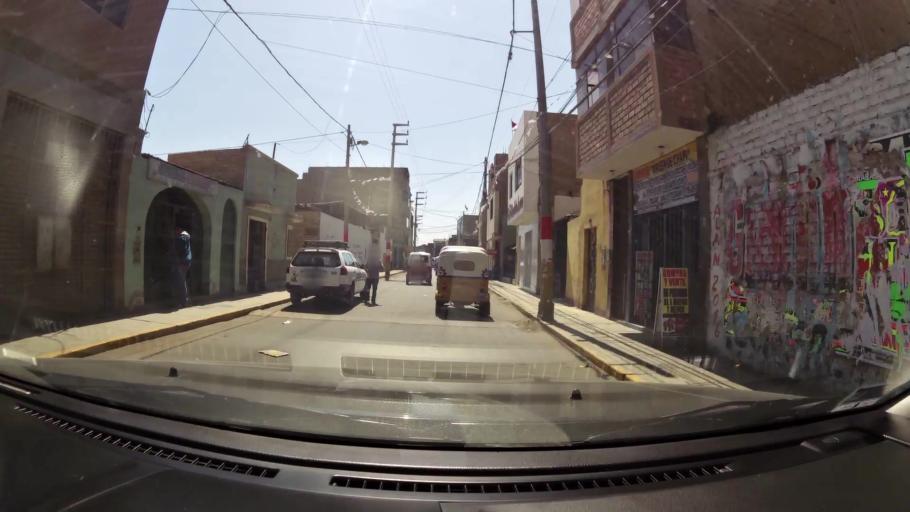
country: PE
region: Ica
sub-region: Provincia de Ica
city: Ica
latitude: -14.0676
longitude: -75.7248
